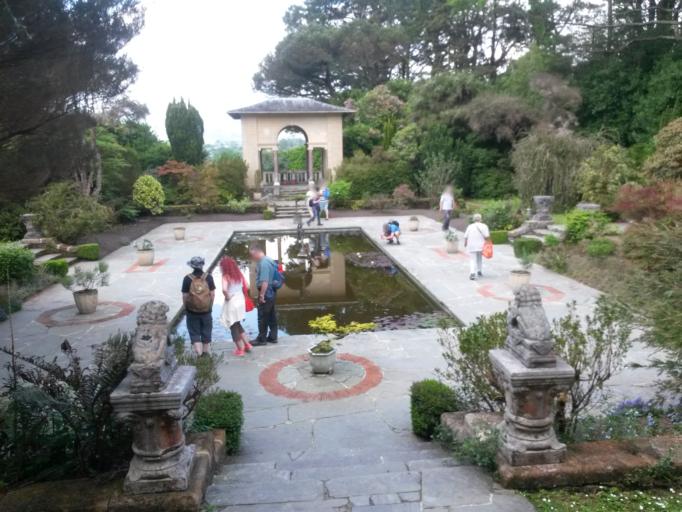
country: IE
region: Munster
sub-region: County Cork
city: Bantry
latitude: 51.7360
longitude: -9.5462
